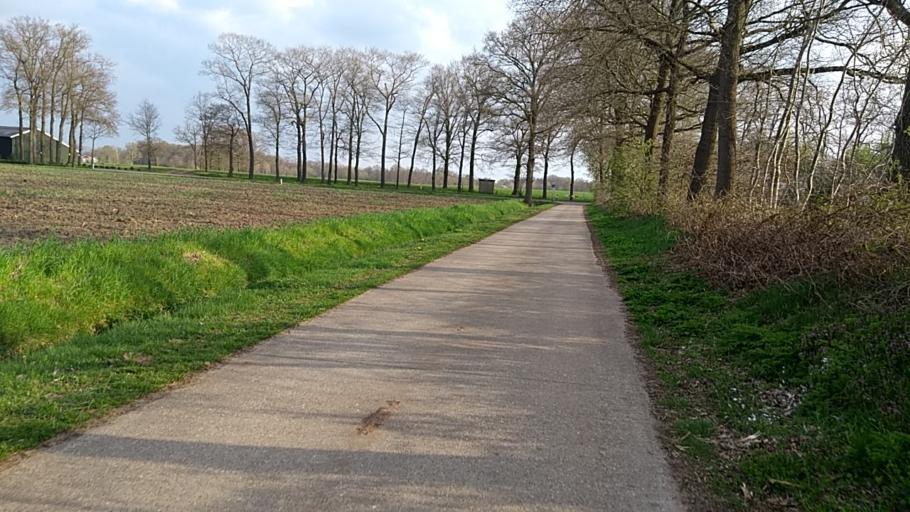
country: NL
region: Overijssel
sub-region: Gemeente Borne
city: Borne
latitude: 52.3450
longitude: 6.7273
